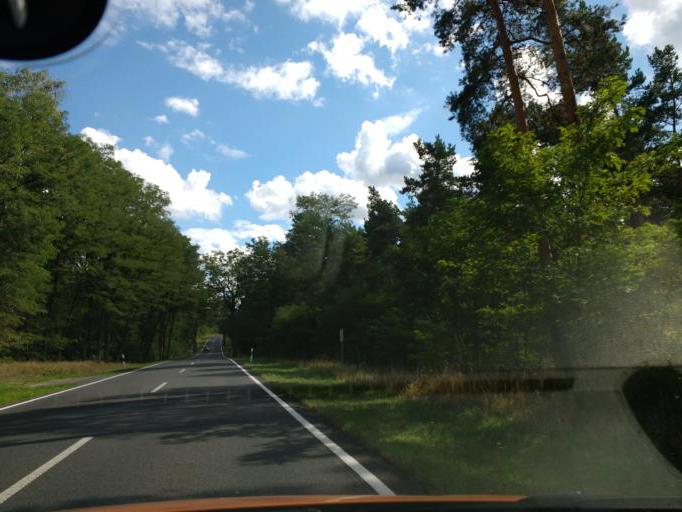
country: DE
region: Brandenburg
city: Wendisch Rietz
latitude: 52.2188
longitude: 13.9822
